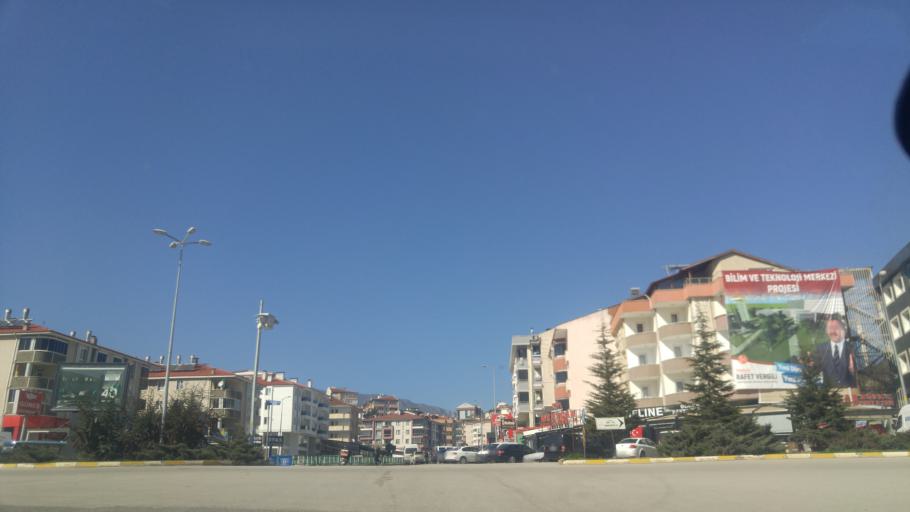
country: TR
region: Karabuk
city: Karabuk
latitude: 41.2180
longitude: 32.6604
